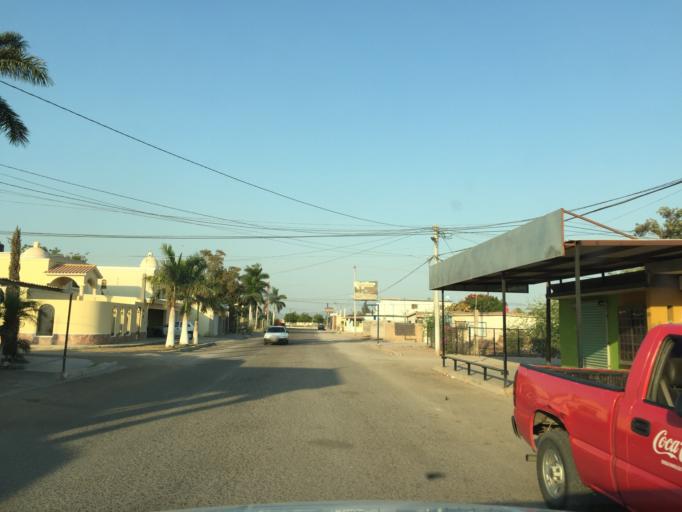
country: MX
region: Sonora
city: Navojoa
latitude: 27.0563
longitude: -109.4574
